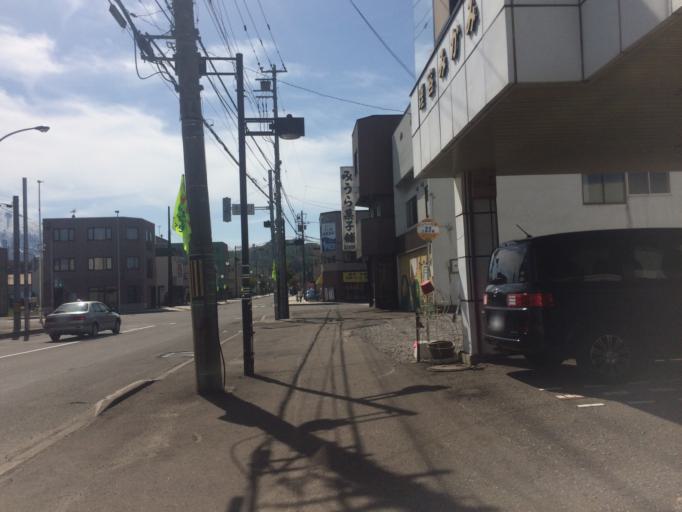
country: JP
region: Hokkaido
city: Niseko Town
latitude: 42.9040
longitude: 140.7535
